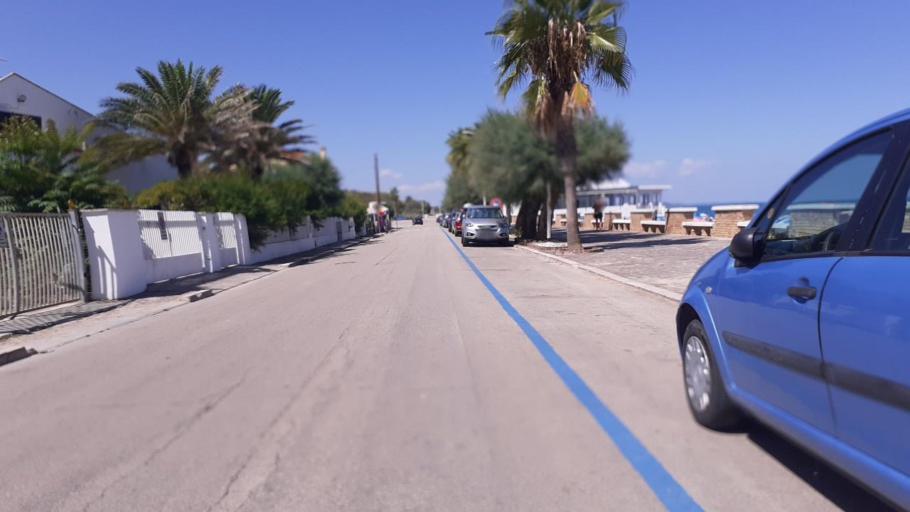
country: IT
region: Abruzzo
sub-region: Provincia di Chieti
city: Casalbordino-Miracoli
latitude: 42.1955
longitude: 14.6309
